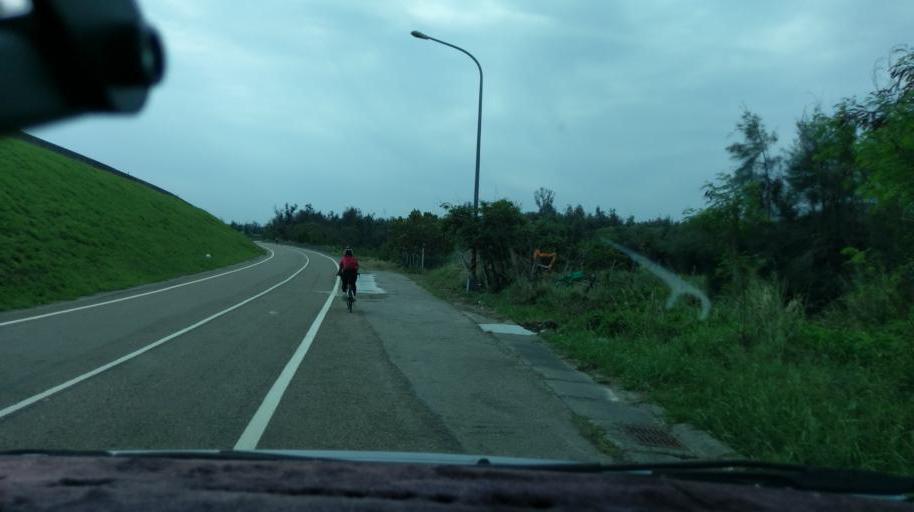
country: TW
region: Taiwan
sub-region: Miaoli
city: Miaoli
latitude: 24.6015
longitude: 120.7432
